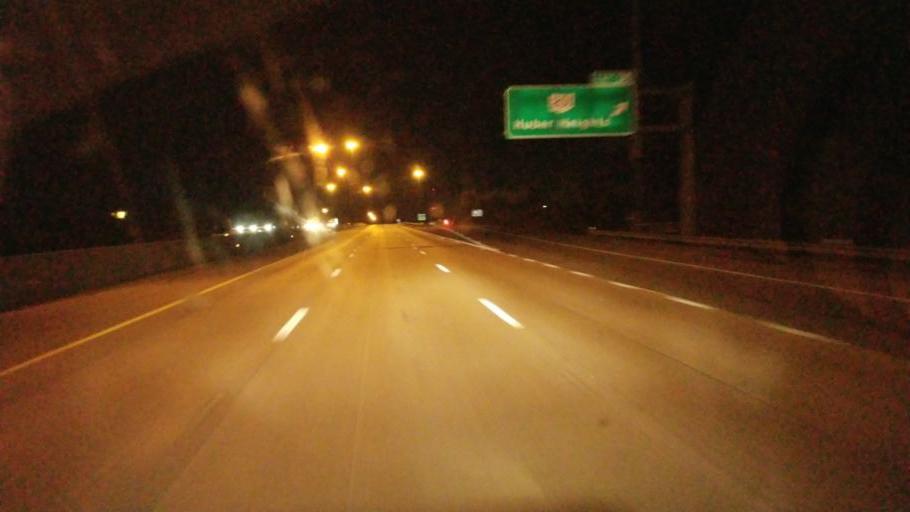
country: US
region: Ohio
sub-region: Montgomery County
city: Huber Heights
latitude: 39.8676
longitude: -84.0950
